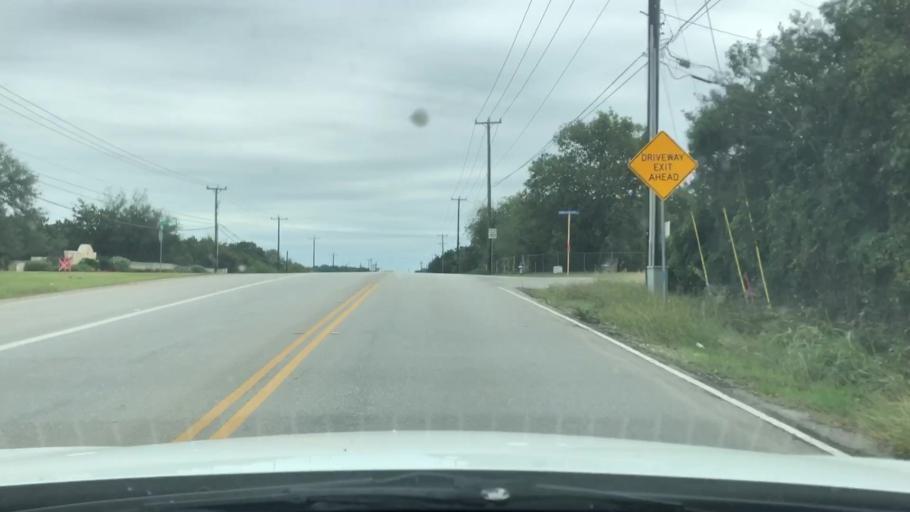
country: US
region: Texas
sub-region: Bexar County
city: Timberwood Park
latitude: 29.6477
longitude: -98.4100
